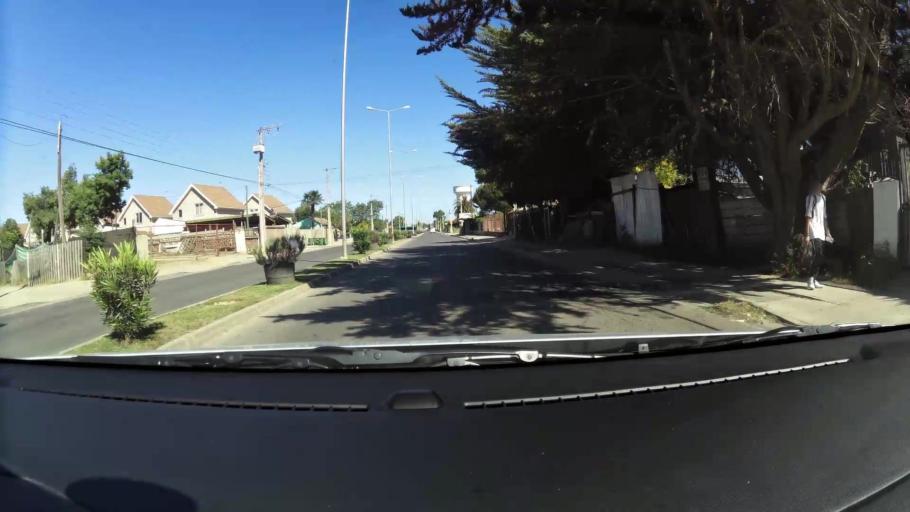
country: CL
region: Valparaiso
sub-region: Provincia de Marga Marga
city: Quilpue
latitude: -33.3266
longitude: -71.3976
